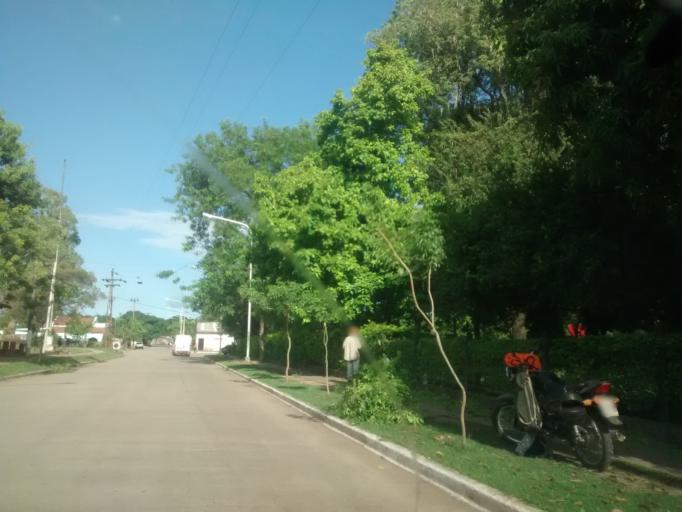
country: AR
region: Chaco
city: Puerto Tirol
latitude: -27.3739
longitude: -59.0882
